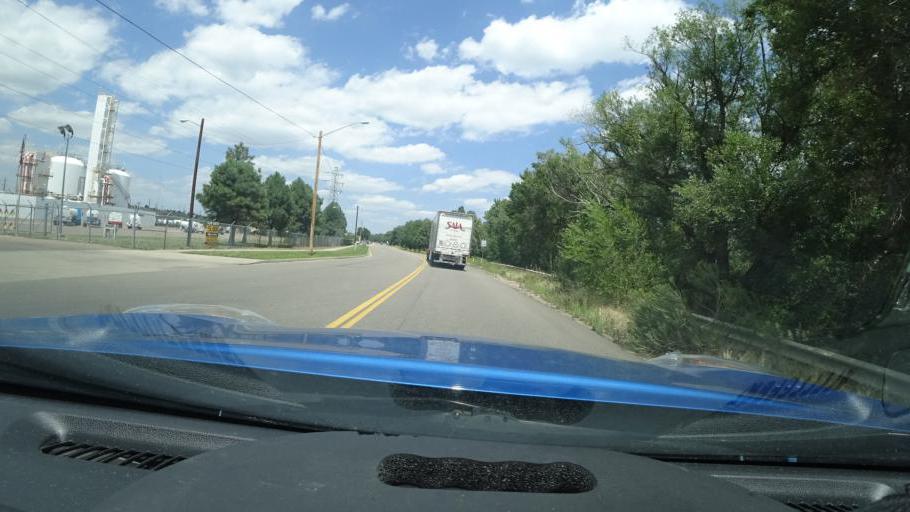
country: US
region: Colorado
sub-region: Arapahoe County
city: Englewood
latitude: 39.6711
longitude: -104.9983
